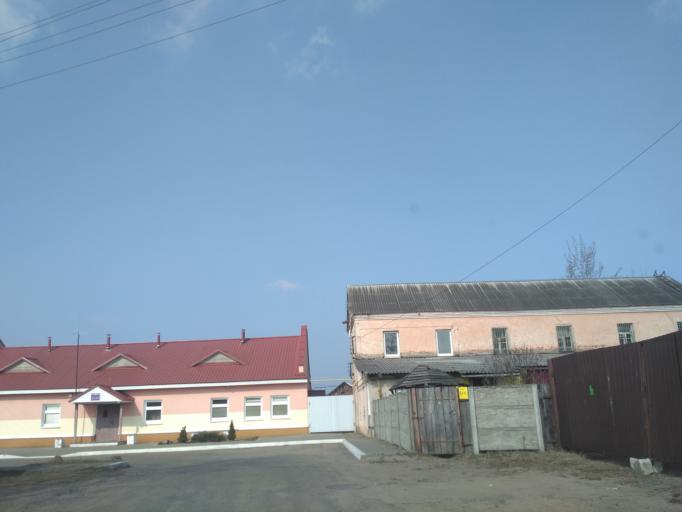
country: BY
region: Minsk
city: Horad Barysaw
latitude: 54.2400
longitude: 28.5020
